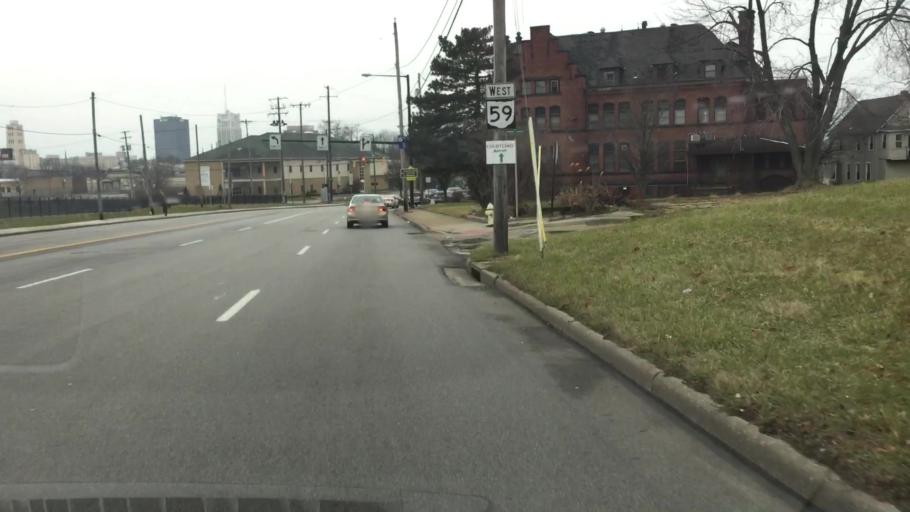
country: US
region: Ohio
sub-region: Summit County
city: Akron
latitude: 41.0839
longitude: -81.5045
